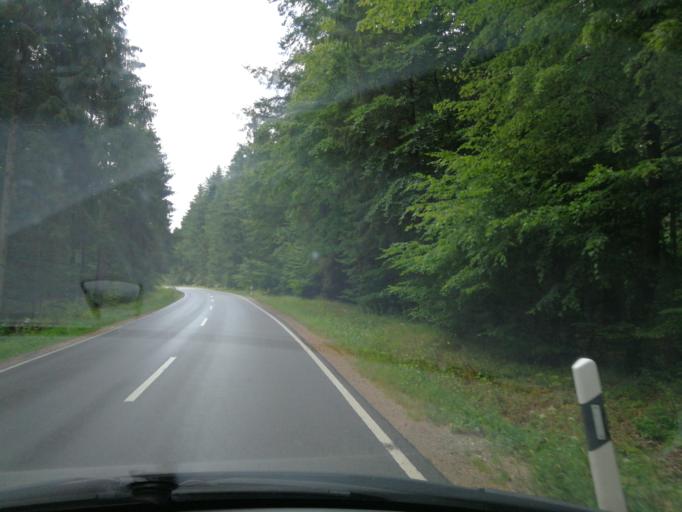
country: DE
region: Bavaria
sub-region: Upper Palatinate
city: Wiesent
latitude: 49.0314
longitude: 12.3713
